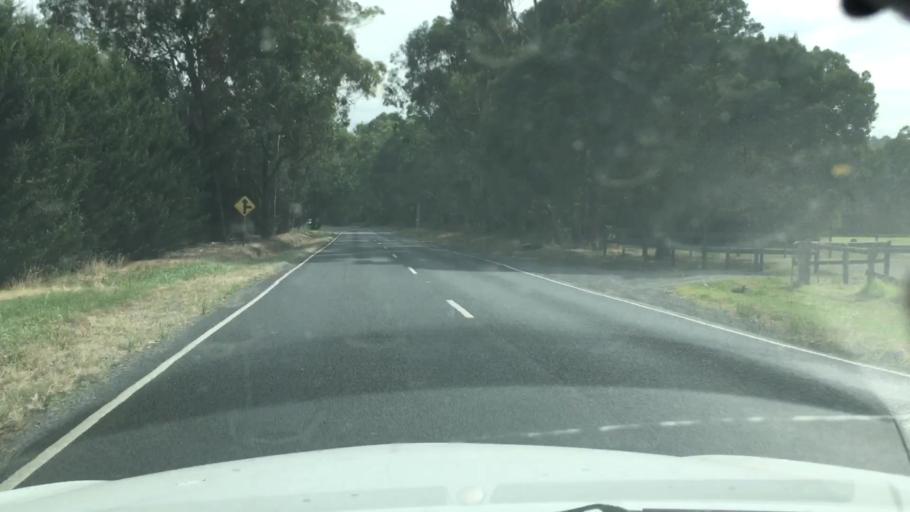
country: AU
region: Victoria
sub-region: Yarra Ranges
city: Woori Yallock
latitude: -37.8051
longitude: 145.5231
